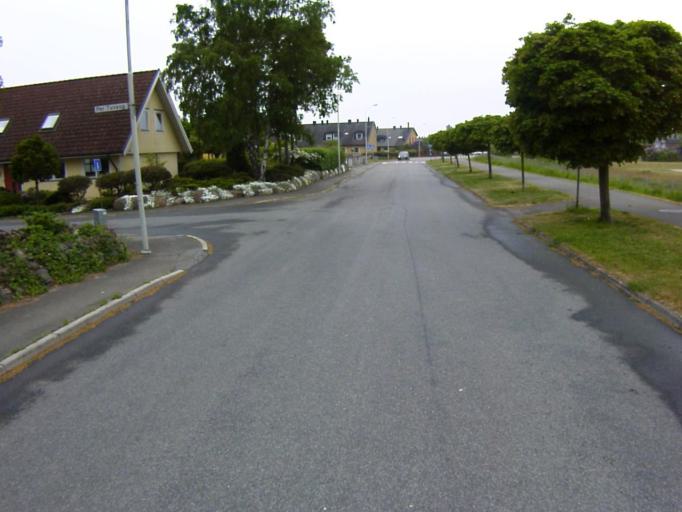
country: SE
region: Skane
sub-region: Kristianstads Kommun
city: Ahus
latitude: 55.9268
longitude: 14.2864
